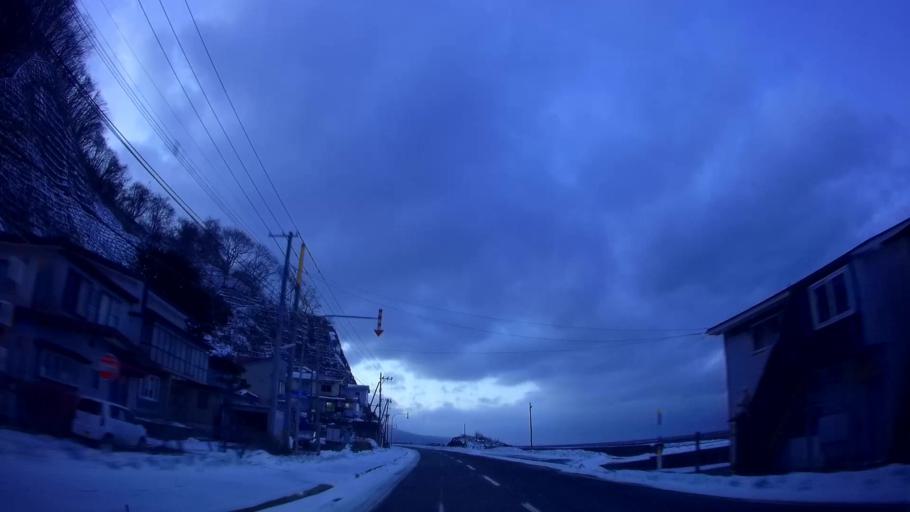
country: JP
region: Hokkaido
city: Hakodate
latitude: 41.8888
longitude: 141.0615
